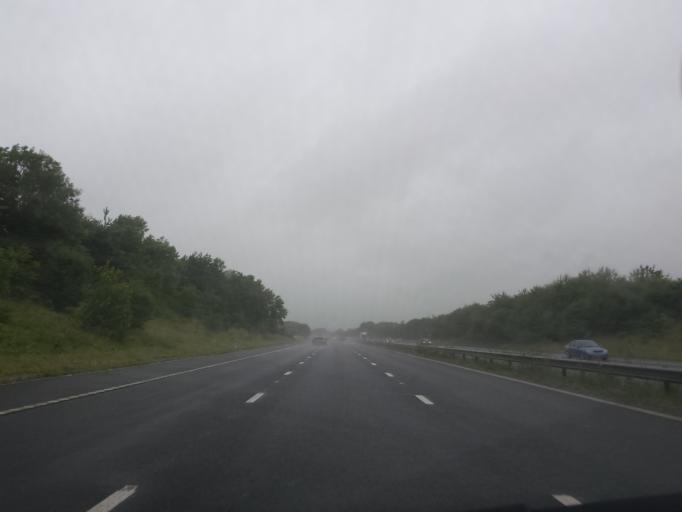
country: GB
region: England
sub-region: Leicestershire
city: Croft
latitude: 52.5844
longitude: -1.2429
